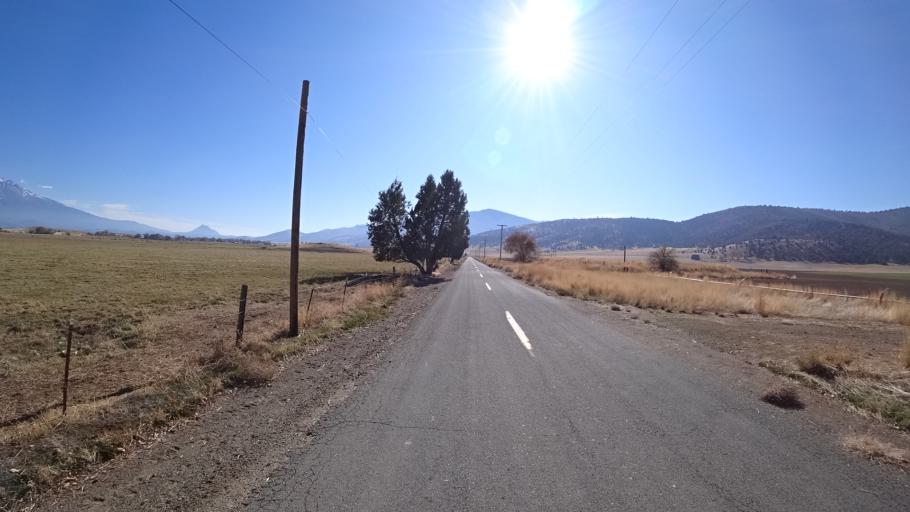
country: US
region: California
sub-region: Siskiyou County
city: Weed
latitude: 41.5339
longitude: -122.5352
